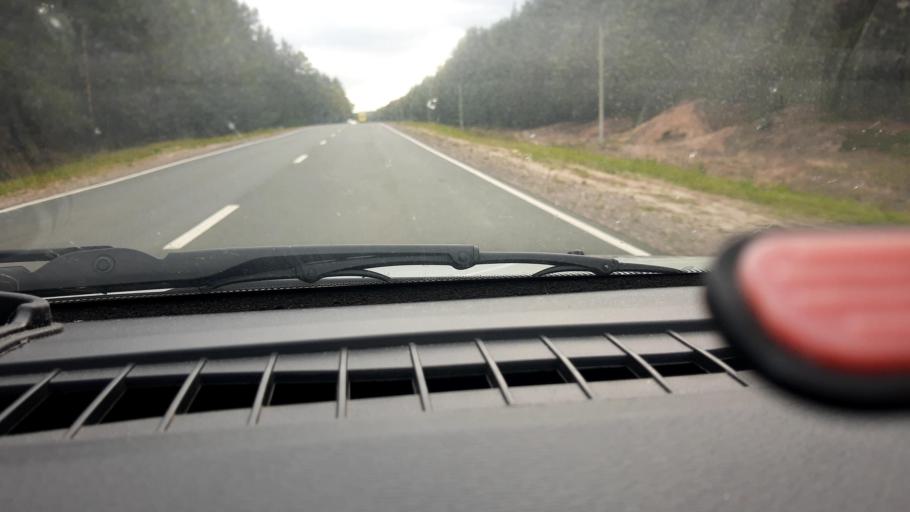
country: RU
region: Nizjnij Novgorod
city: Uren'
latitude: 57.4245
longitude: 45.6898
